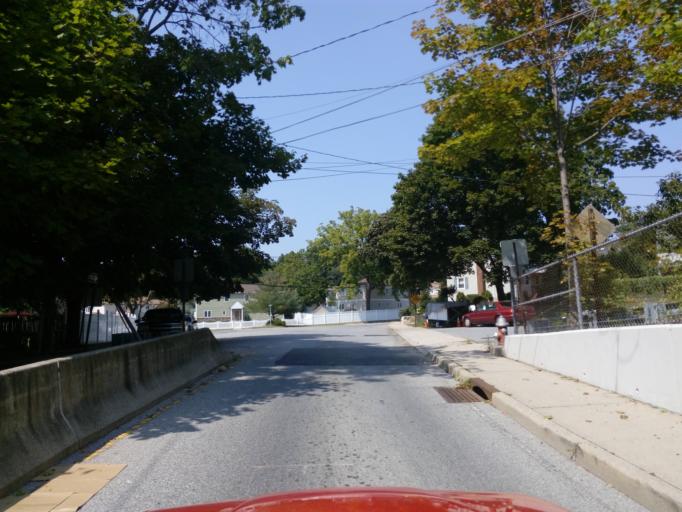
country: US
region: New York
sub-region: Nassau County
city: Glen Cove
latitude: 40.8644
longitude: -73.6353
